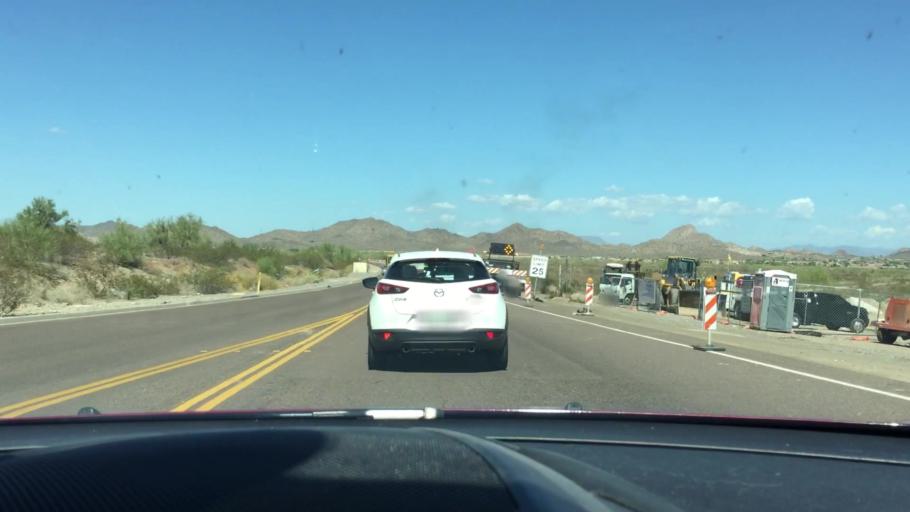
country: US
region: Arizona
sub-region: Maricopa County
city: Sun City West
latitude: 33.7102
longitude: -112.2350
